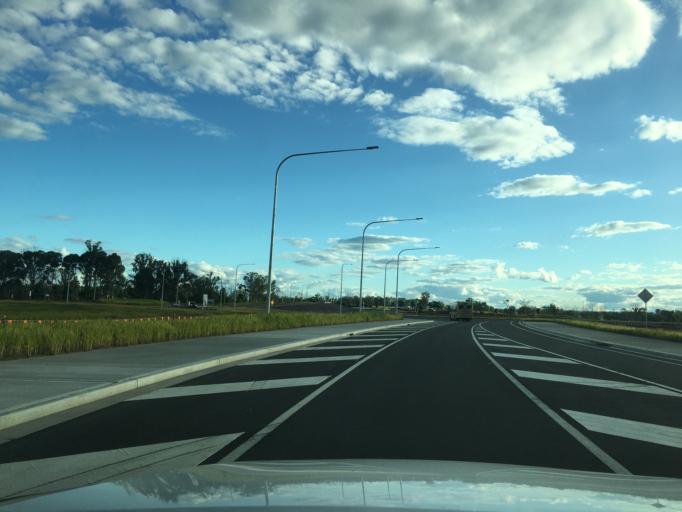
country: AU
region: New South Wales
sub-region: Liverpool
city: Bringelly
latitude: -33.8818
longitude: 150.7441
